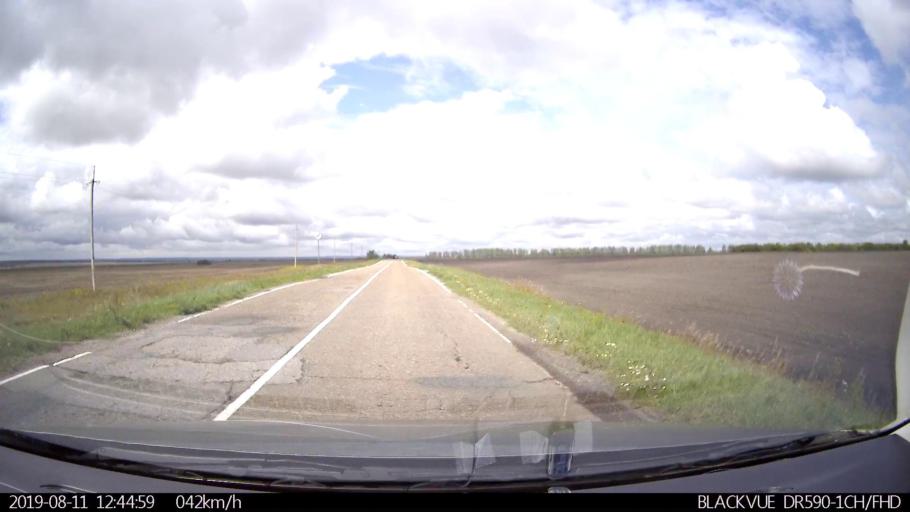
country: RU
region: Ulyanovsk
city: Ignatovka
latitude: 53.8574
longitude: 47.7325
